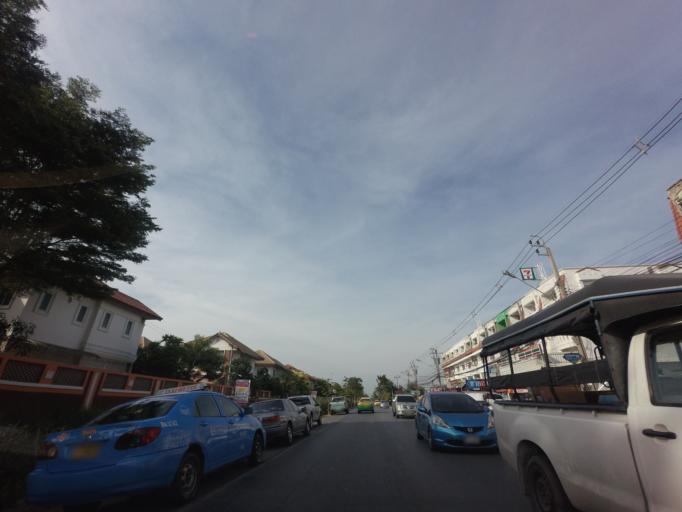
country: TH
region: Bangkok
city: Khan Na Yao
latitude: 13.8614
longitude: 100.6928
